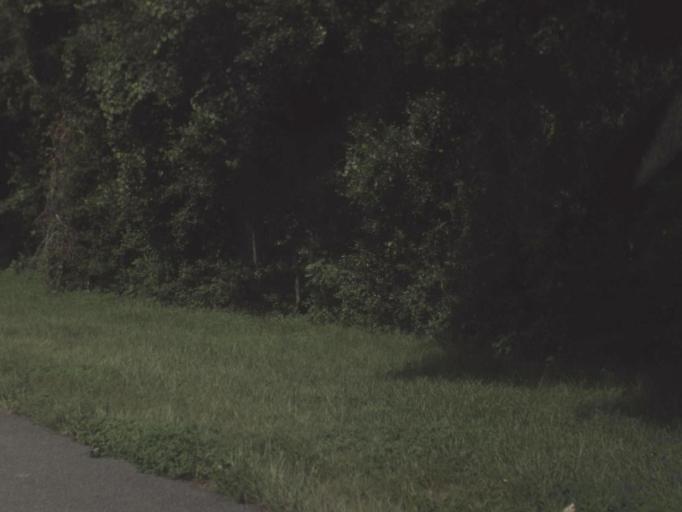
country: US
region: Florida
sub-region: Pasco County
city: Saint Leo
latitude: 28.3398
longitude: -82.2334
